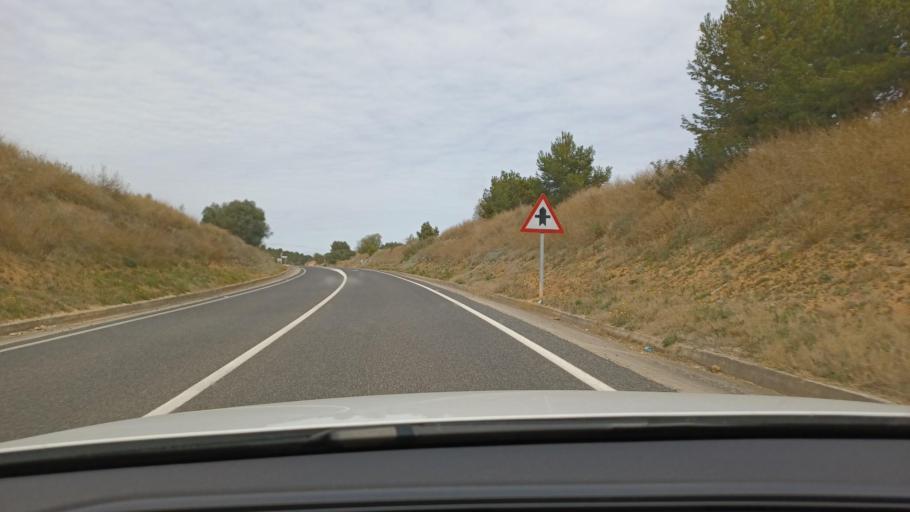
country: ES
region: Catalonia
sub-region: Provincia de Tarragona
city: Masdenverge
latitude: 40.6746
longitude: 0.5265
